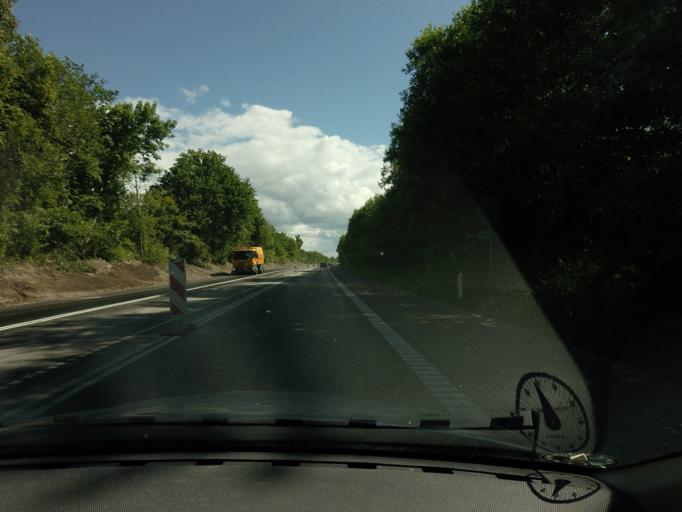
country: DK
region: Central Jutland
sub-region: Syddjurs Kommune
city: Hornslet
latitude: 56.2977
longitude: 10.3393
